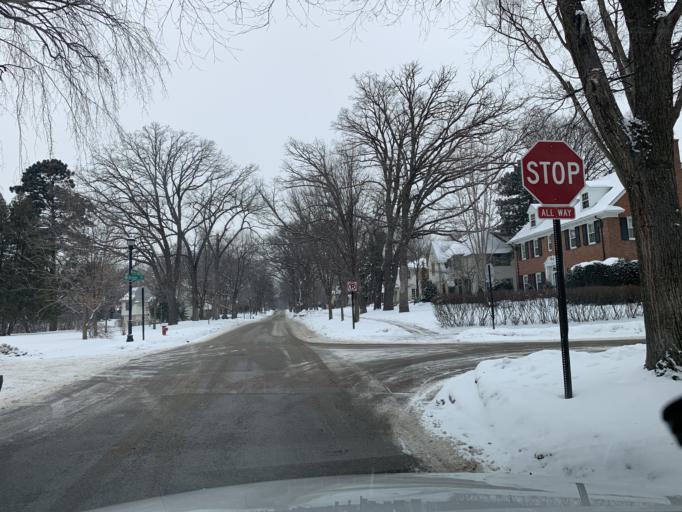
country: US
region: Minnesota
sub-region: Hennepin County
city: Edina
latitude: 44.9163
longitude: -93.3438
